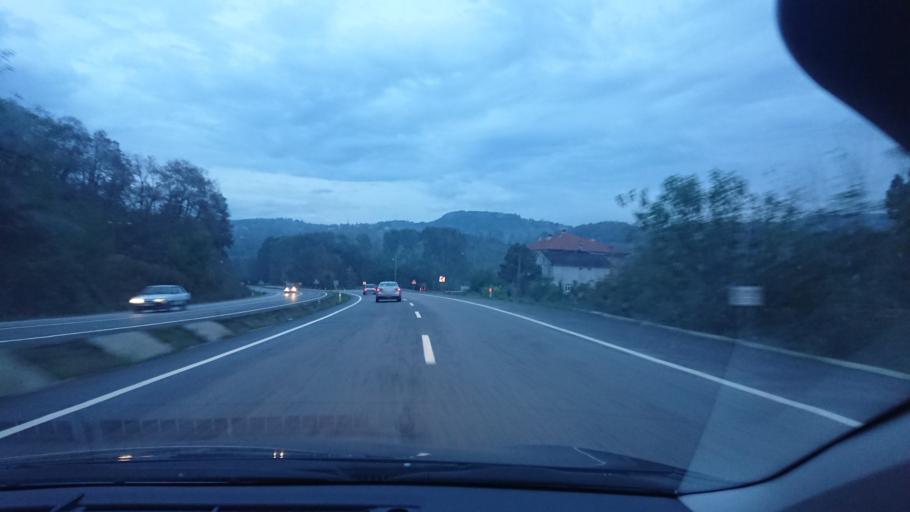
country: TR
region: Zonguldak
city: Beycuma
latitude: 41.3245
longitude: 32.0484
